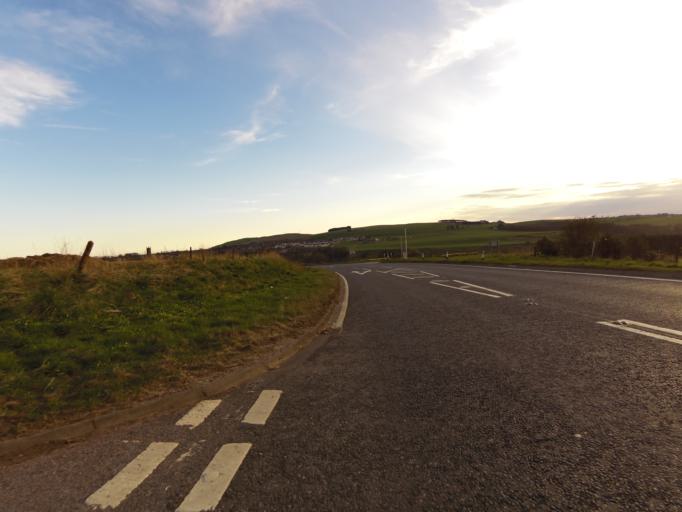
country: GB
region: Scotland
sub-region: Aberdeenshire
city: Inverbervie
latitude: 56.8510
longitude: -2.2781
